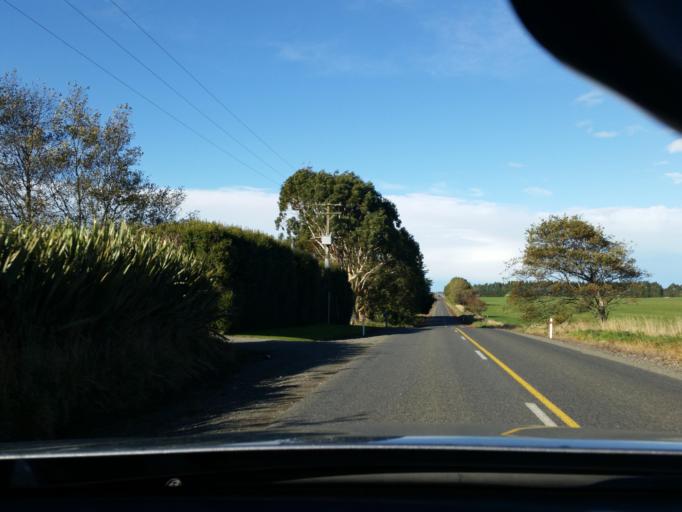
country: NZ
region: Southland
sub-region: Southland District
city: Riverton
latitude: -46.1770
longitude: 168.1098
